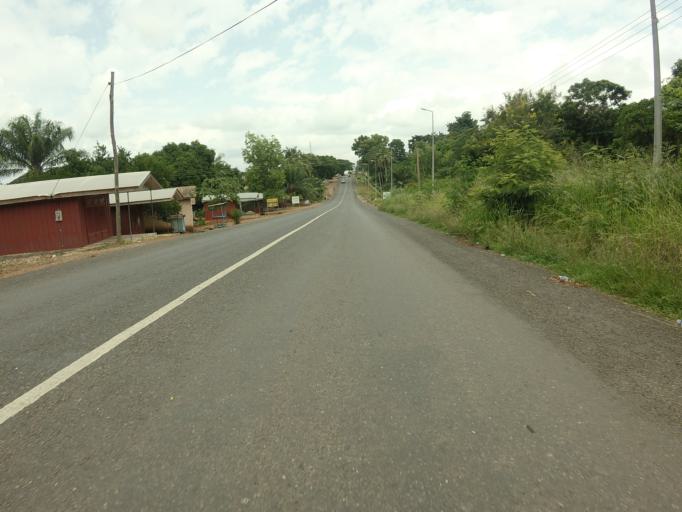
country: GH
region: Volta
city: Ho
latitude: 6.6079
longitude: 0.4655
